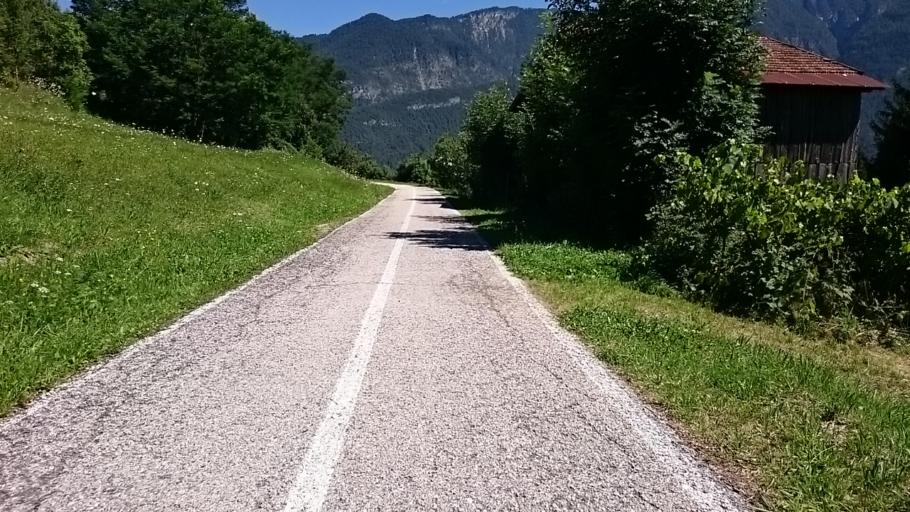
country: IT
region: Veneto
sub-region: Provincia di Belluno
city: Pieve di Cadore
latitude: 46.4248
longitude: 12.3677
